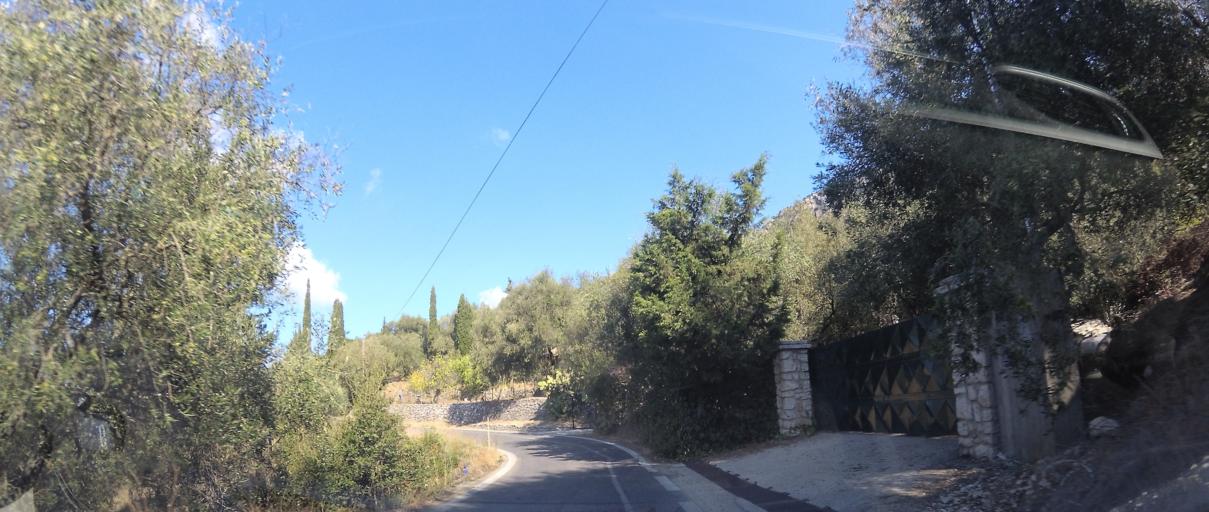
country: GR
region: Ionian Islands
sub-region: Nomos Kerkyras
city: Acharavi
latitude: 39.7233
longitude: 19.8338
